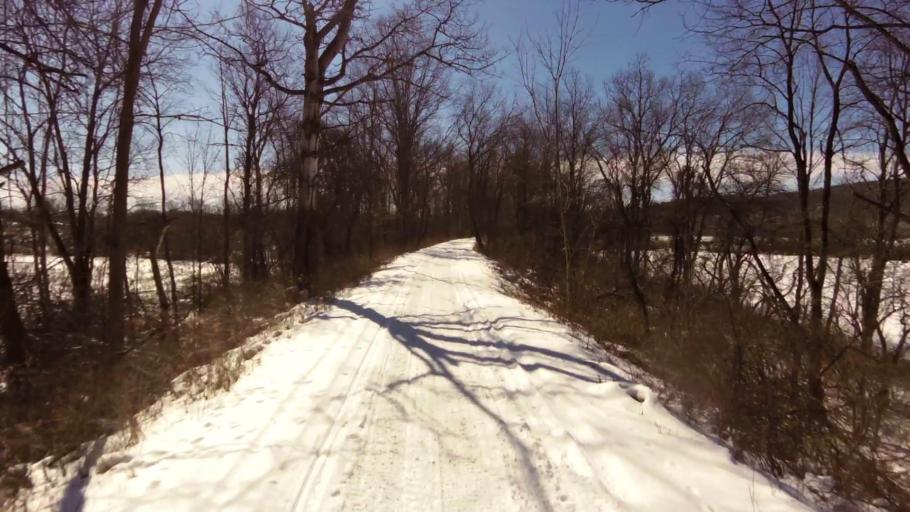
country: US
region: New York
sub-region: Allegany County
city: Houghton
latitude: 42.3524
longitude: -78.1254
